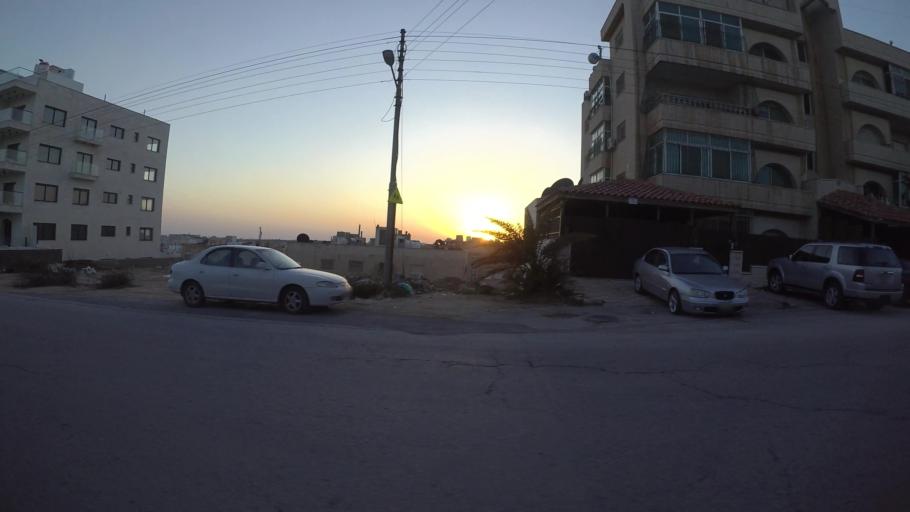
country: JO
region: Amman
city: Al Jubayhah
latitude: 31.9996
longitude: 35.8527
